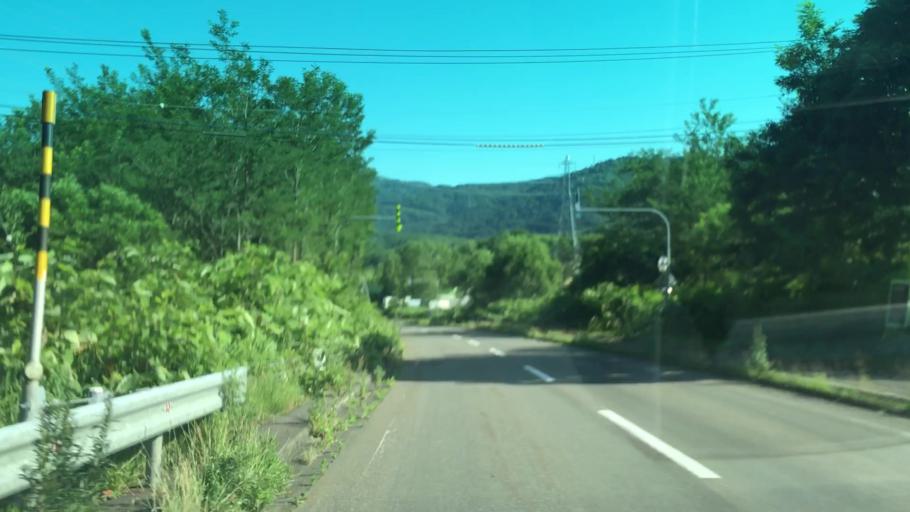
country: JP
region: Hokkaido
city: Yoichi
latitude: 43.0605
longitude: 140.7132
